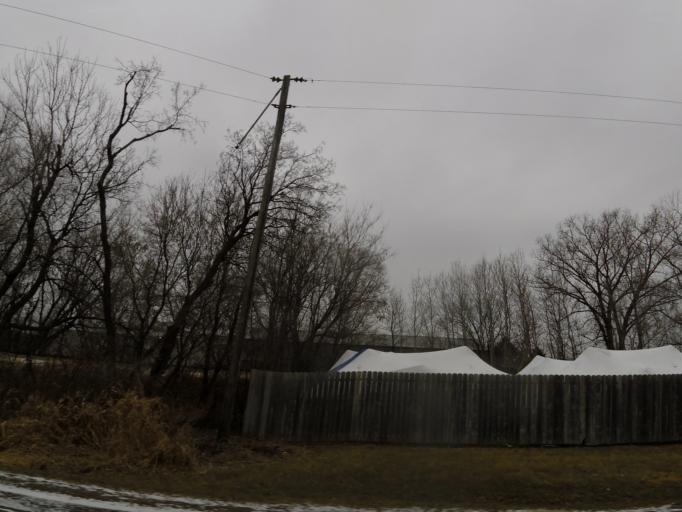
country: US
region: Minnesota
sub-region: Hennepin County
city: Independence
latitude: 45.0125
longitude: -93.6897
